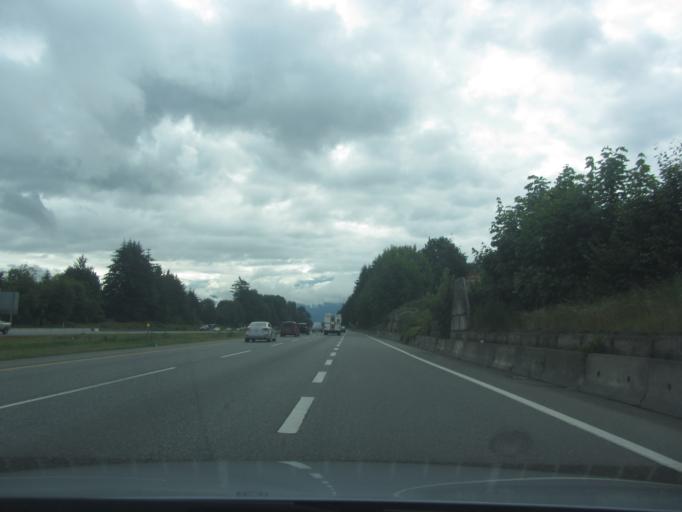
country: US
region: Washington
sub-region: Whatcom County
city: Sumas
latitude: 49.0336
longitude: -122.2870
